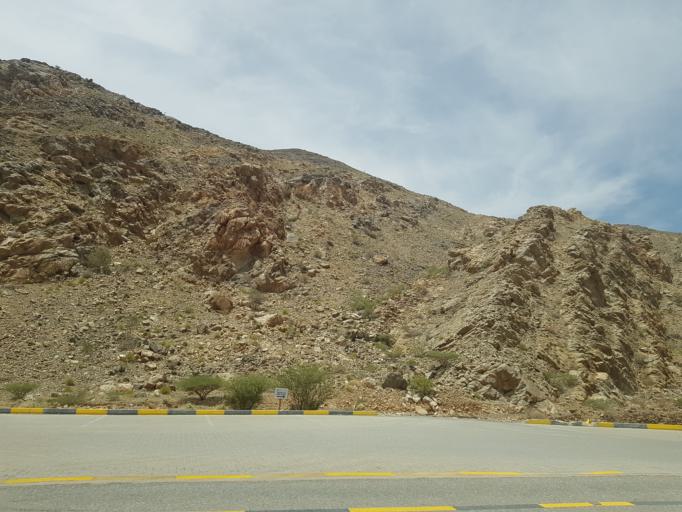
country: OM
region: Muhafazat ad Dakhiliyah
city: Izki
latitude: 22.9610
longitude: 57.6781
